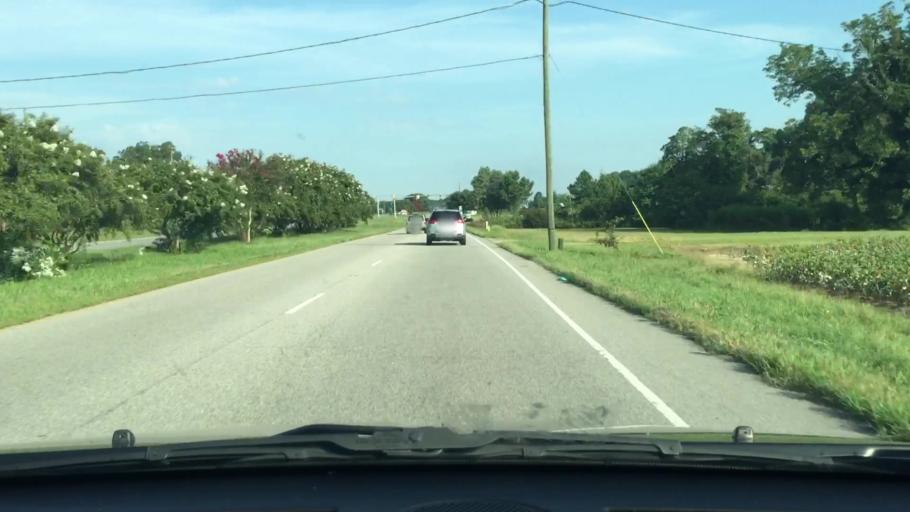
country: US
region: Virginia
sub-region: Isle of Wight County
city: Carrollton
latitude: 36.9477
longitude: -76.5947
